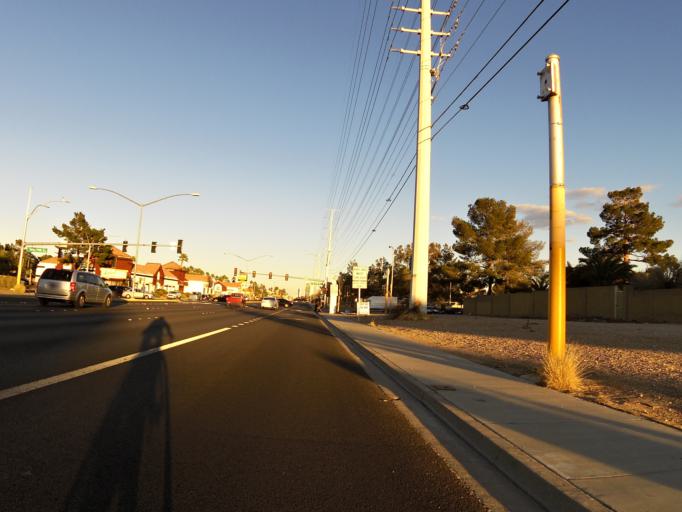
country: US
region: Nevada
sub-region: Clark County
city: Spring Valley
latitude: 36.1144
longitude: -115.2348
